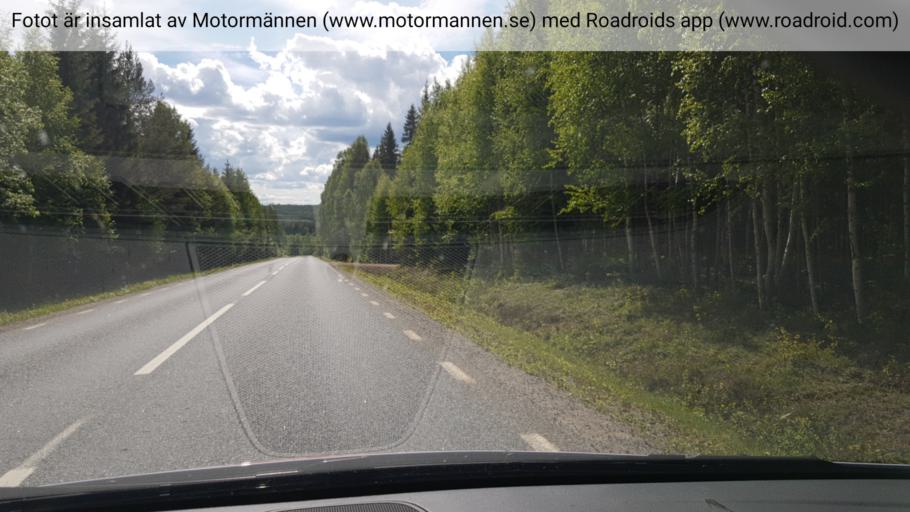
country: SE
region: Vaesterbotten
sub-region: Skelleftea Kommun
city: Burtraesk
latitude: 64.4327
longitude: 20.3983
